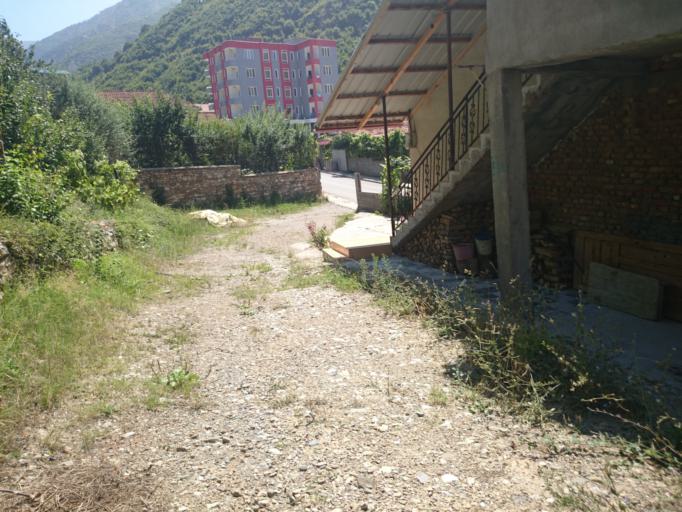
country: AL
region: Diber
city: Peshkopi
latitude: 41.6859
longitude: 20.4428
